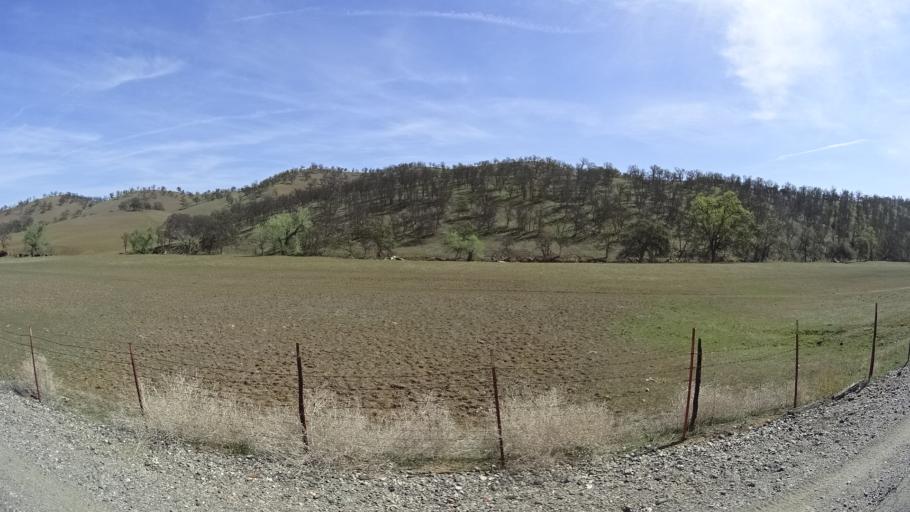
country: US
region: California
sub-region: Glenn County
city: Willows
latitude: 39.5108
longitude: -122.4553
